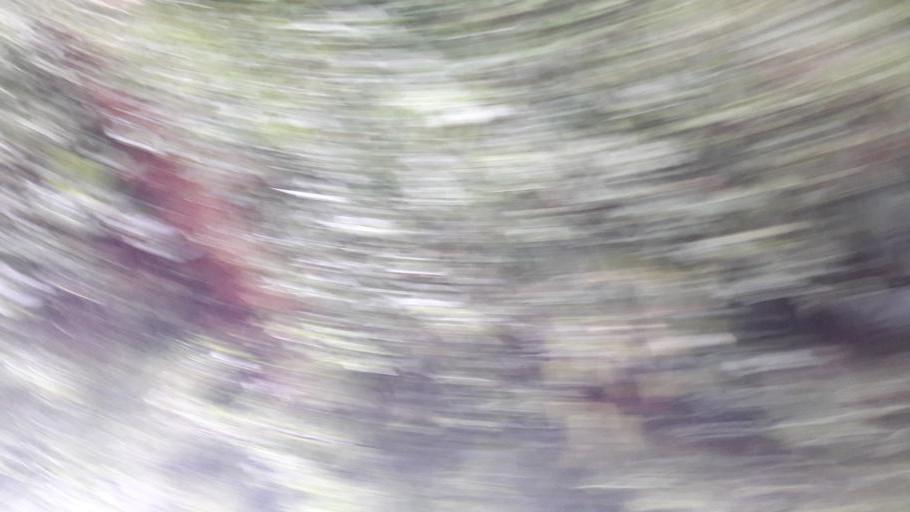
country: ID
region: West Java
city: Cipeundeuy
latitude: -6.6795
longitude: 106.5205
